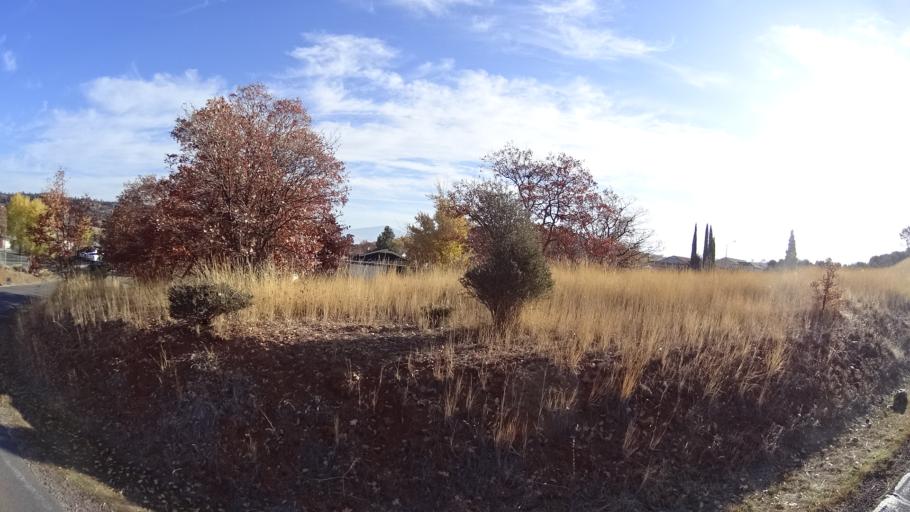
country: US
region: California
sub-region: Siskiyou County
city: Yreka
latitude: 41.7082
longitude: -122.6240
